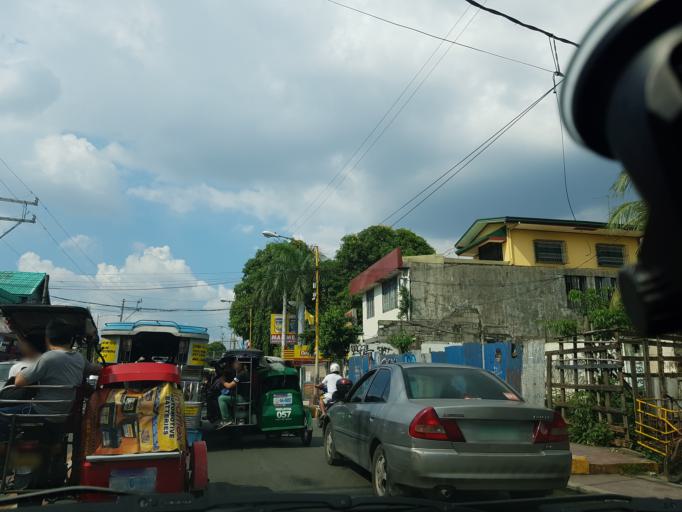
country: PH
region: Calabarzon
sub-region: Province of Rizal
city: Pateros
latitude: 14.5673
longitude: 121.0858
